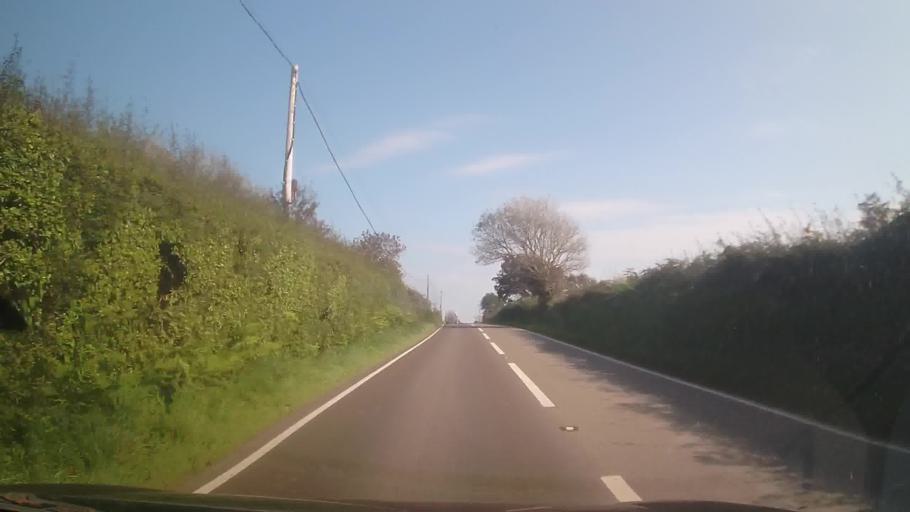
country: GB
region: Wales
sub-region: Pembrokeshire
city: Nevern
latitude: 52.0094
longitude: -4.7298
